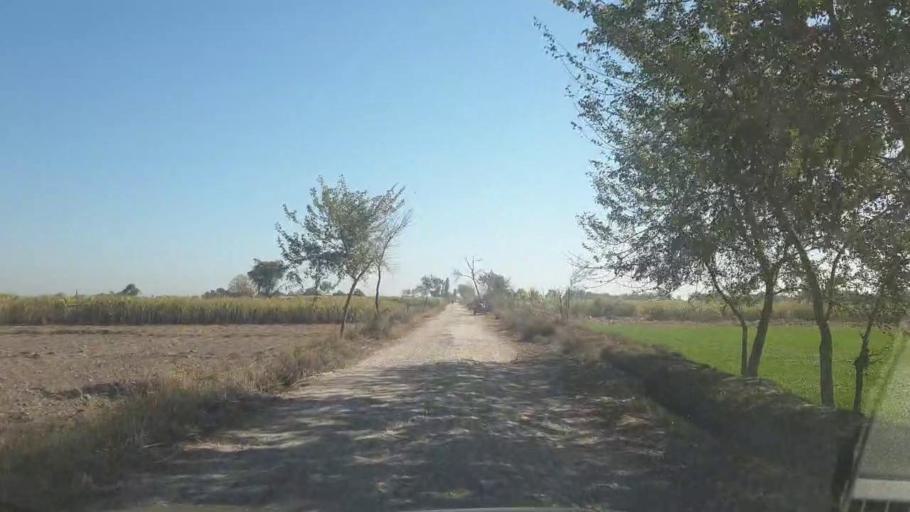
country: PK
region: Sindh
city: Ghotki
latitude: 27.9749
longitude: 69.3328
